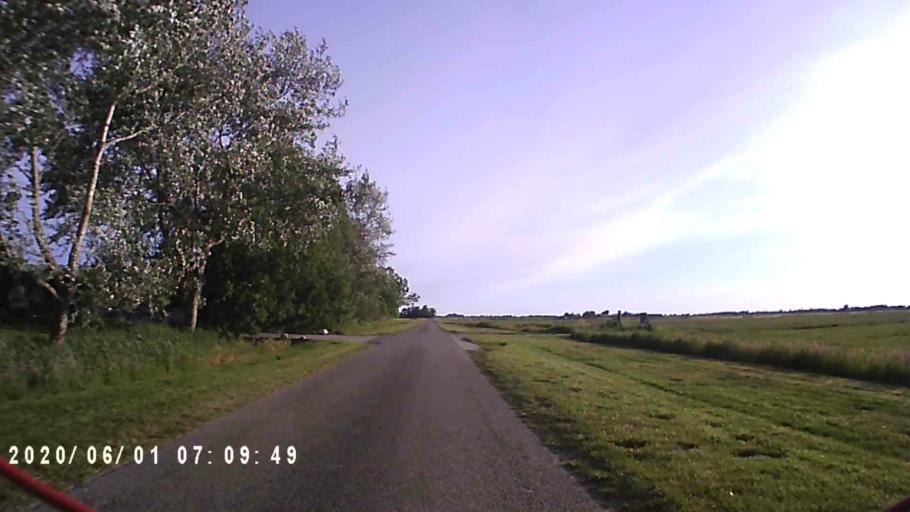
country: NL
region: Friesland
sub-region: Gemeente Dantumadiel
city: Walterswald
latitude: 53.3062
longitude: 6.0721
